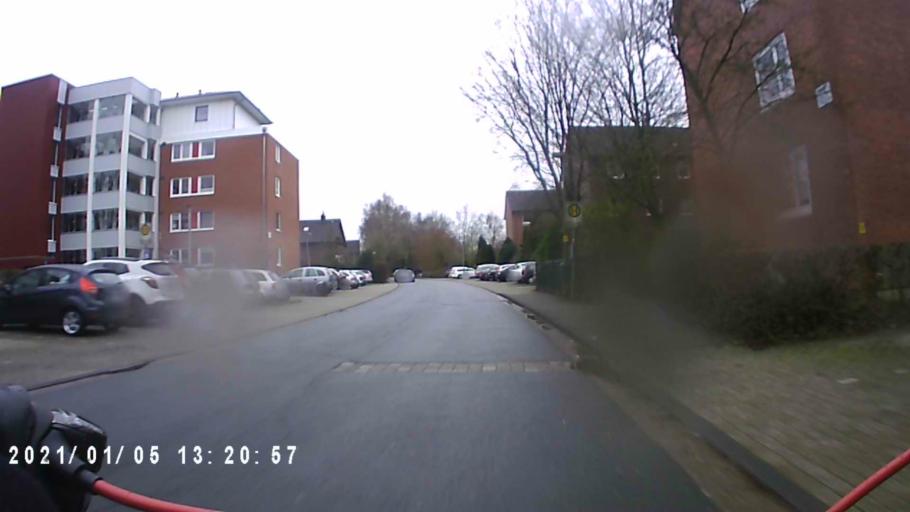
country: DE
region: Lower Saxony
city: Leer
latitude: 53.2336
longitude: 7.4385
